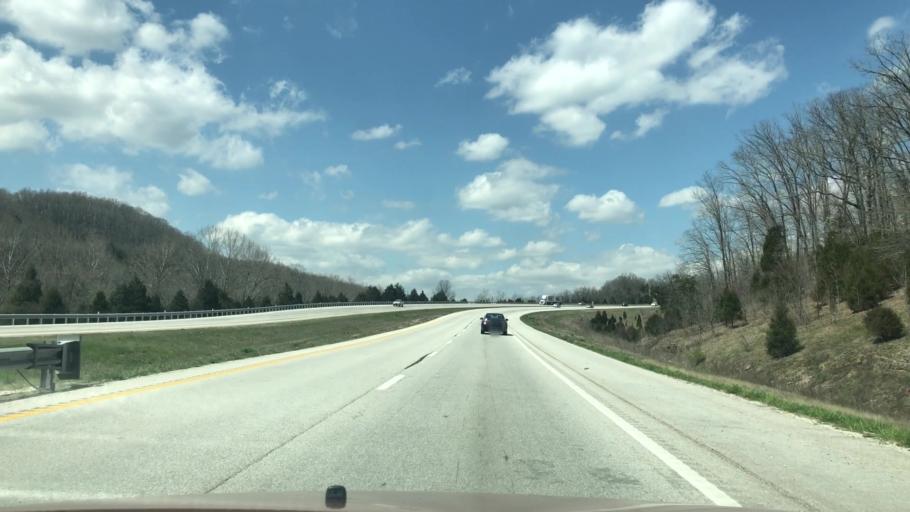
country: US
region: Missouri
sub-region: Christian County
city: Ozark
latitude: 36.9099
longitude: -93.2433
